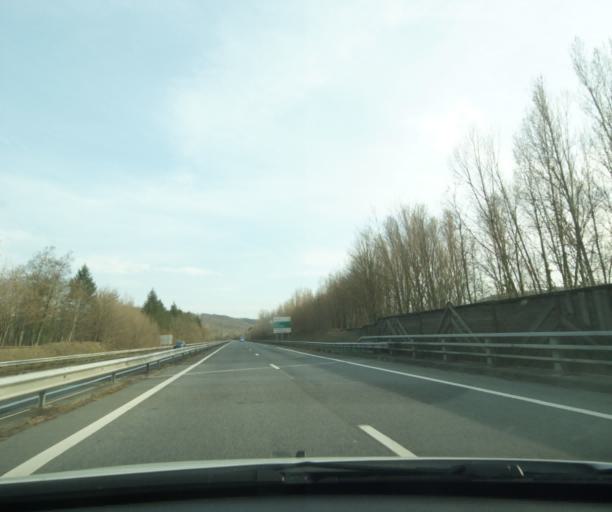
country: FR
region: Midi-Pyrenees
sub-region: Departement des Hautes-Pyrenees
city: Tournay
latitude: 43.1688
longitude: 0.2494
